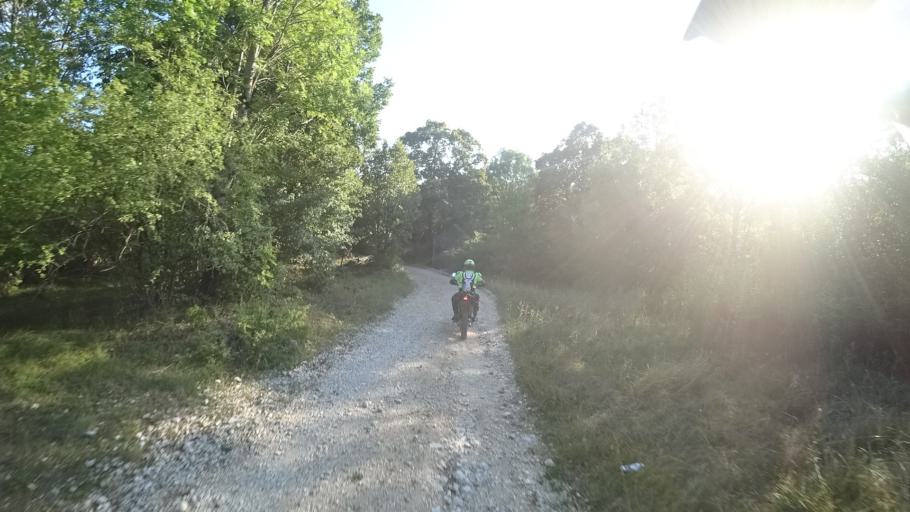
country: HR
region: Sibensko-Kniniska
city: Knin
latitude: 44.1561
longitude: 16.0924
